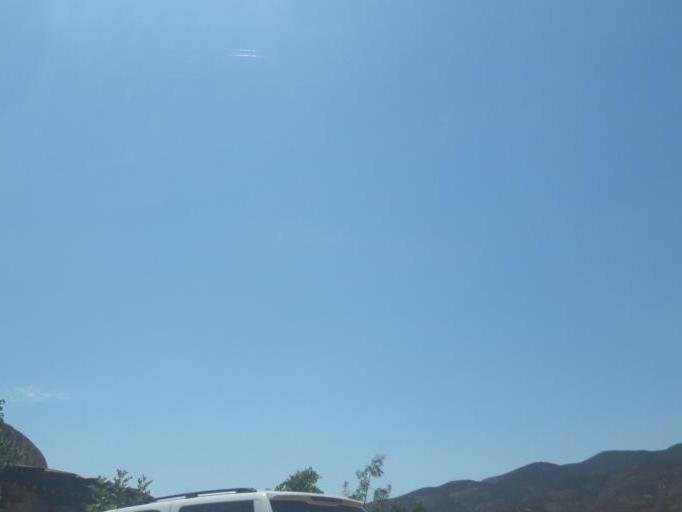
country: MX
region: Baja California
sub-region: Ensenada
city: Rancho Verde
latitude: 32.0935
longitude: -116.6327
